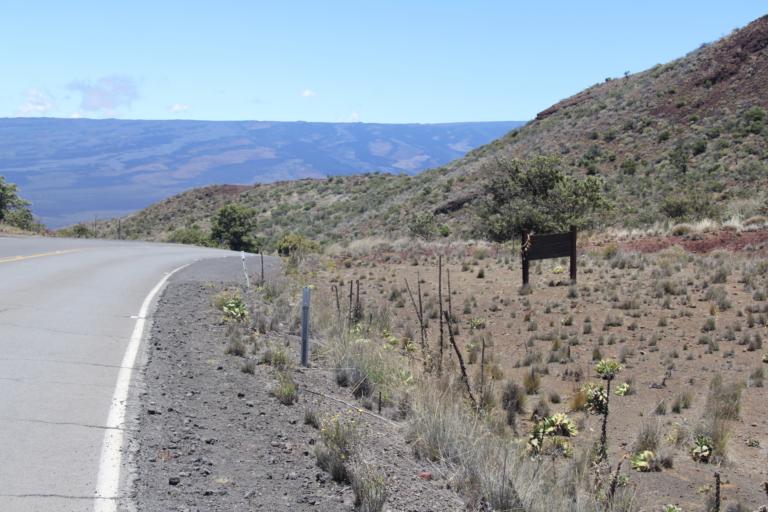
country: US
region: Hawaii
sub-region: Hawaii County
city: Honoka'a
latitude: 19.7573
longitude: -155.4563
